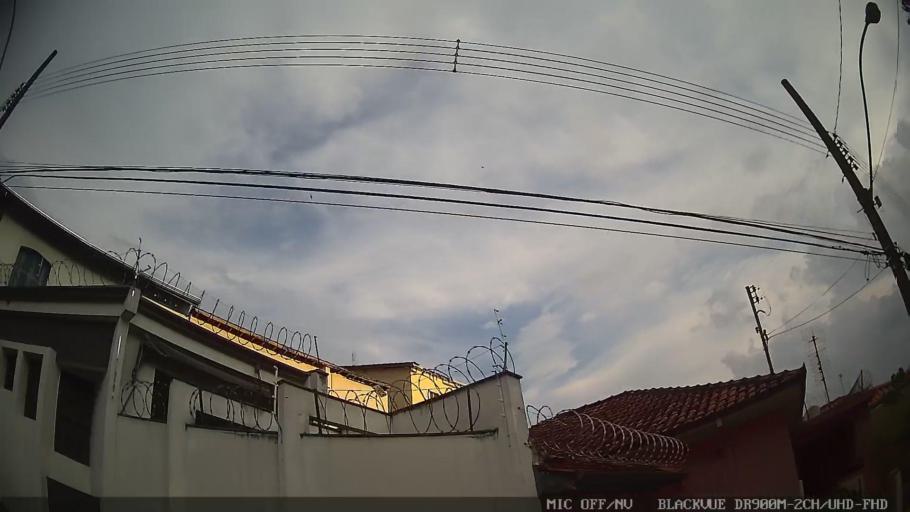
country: BR
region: Sao Paulo
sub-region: Braganca Paulista
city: Braganca Paulista
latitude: -22.9490
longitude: -46.5398
